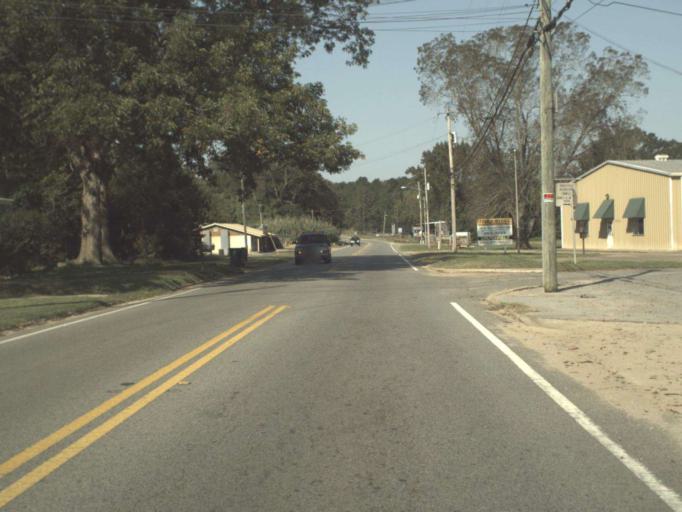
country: US
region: Florida
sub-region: Jackson County
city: Graceville
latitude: 30.9636
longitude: -85.5199
